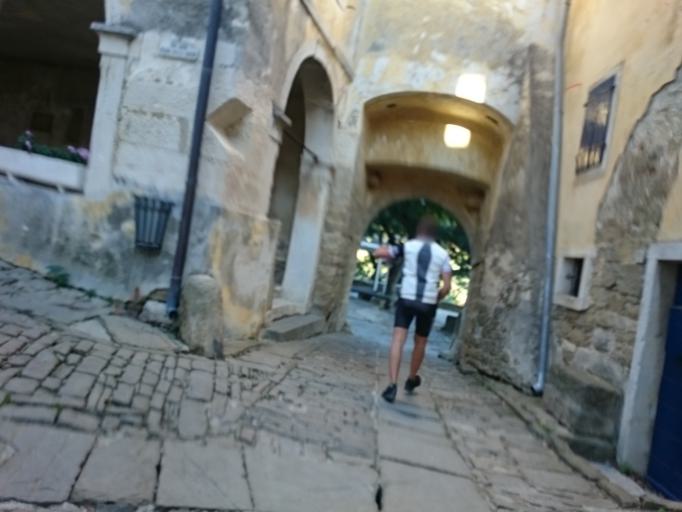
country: HR
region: Istarska
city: Buje
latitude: 45.3790
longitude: 13.7232
